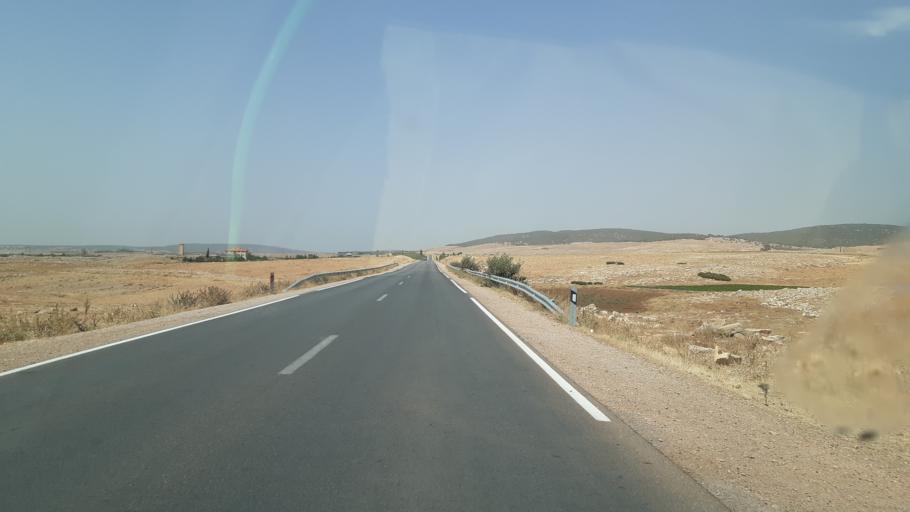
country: MA
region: Meknes-Tafilalet
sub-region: Ifrane
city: Ifrane
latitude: 33.5966
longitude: -5.0858
